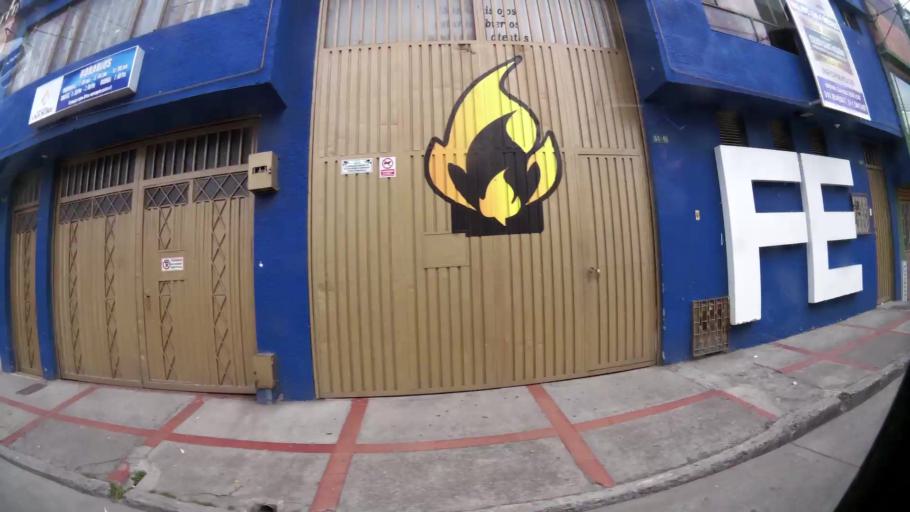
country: CO
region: Cundinamarca
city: Funza
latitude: 4.7045
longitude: -74.1357
